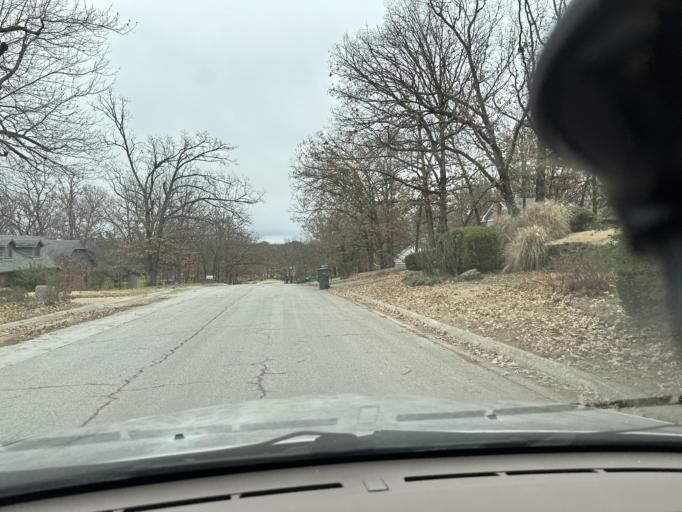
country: US
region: Arkansas
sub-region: Washington County
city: Johnson
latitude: 36.1029
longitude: -94.1430
